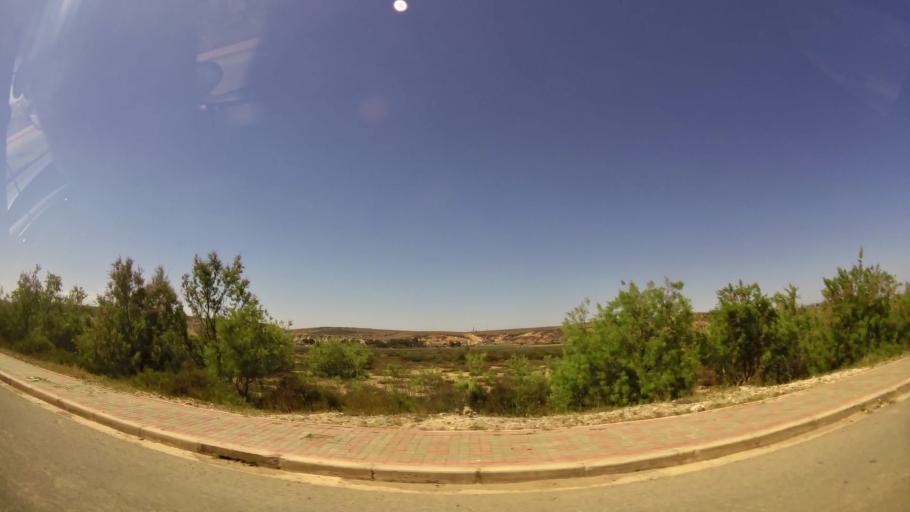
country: MA
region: Oriental
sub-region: Berkane-Taourirt
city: Madagh
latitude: 35.0996
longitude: -2.3072
